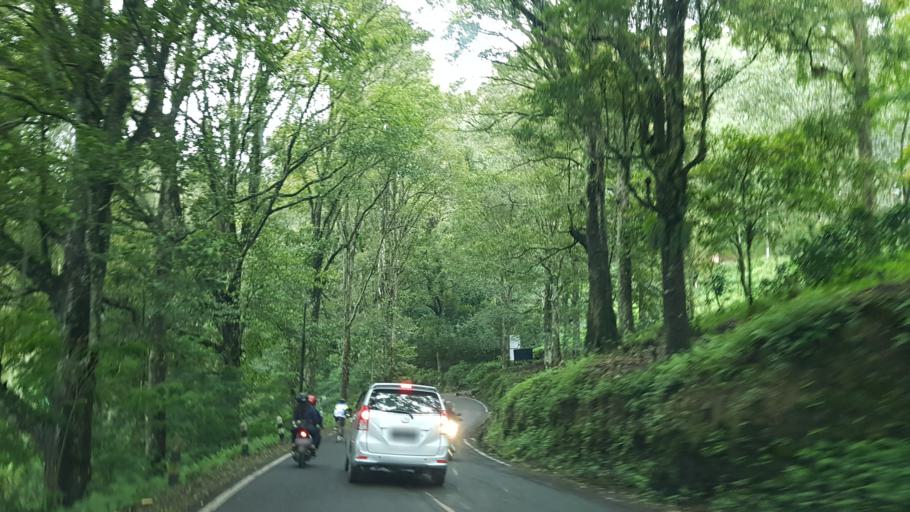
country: ID
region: West Java
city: Banjar
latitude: -7.1329
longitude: 107.4129
